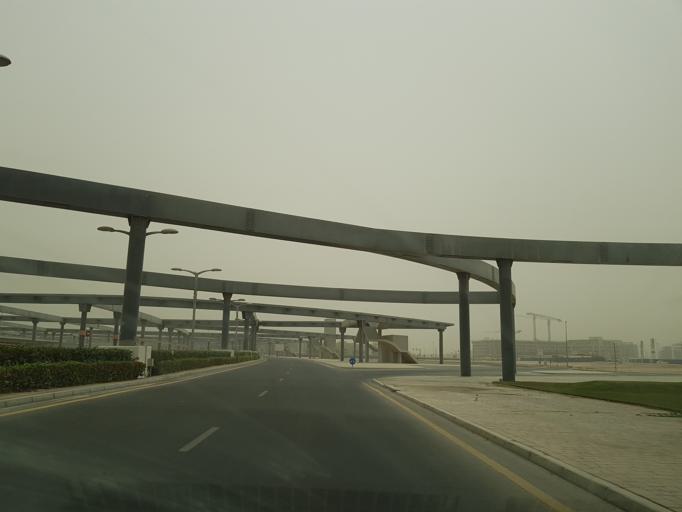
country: AE
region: Dubai
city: Dubai
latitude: 25.1585
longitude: 55.2976
